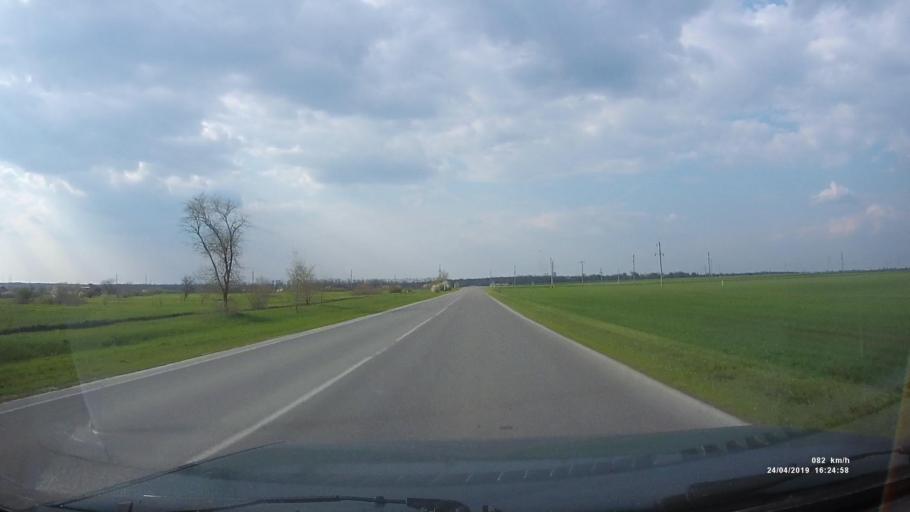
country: RU
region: Rostov
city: Orlovskiy
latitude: 46.8473
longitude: 42.0445
